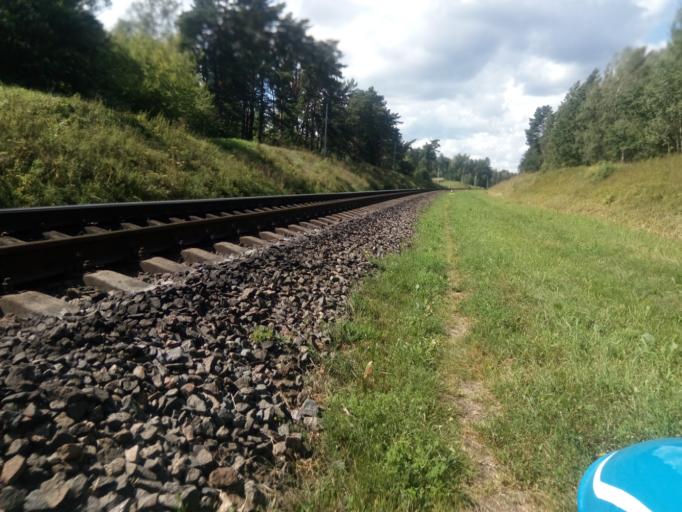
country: BY
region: Vitebsk
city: Dzisna
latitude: 55.6793
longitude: 28.2926
